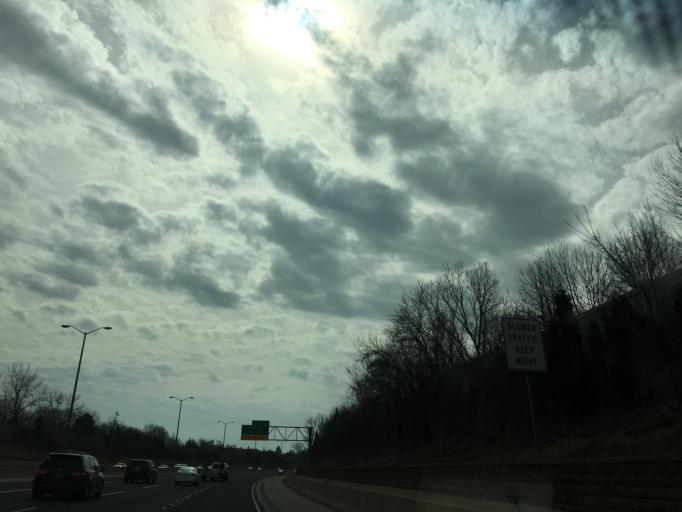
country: US
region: Illinois
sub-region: DuPage County
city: Woodridge
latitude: 41.7633
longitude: -88.0375
